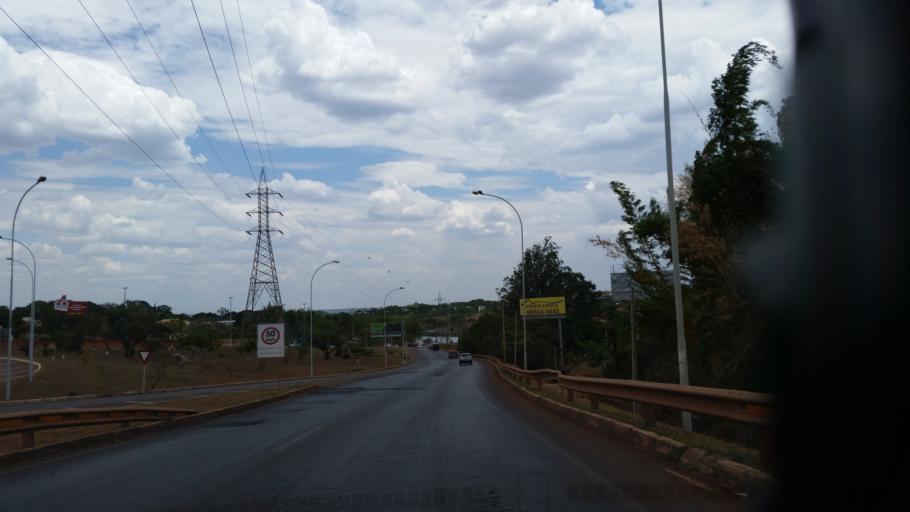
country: BR
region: Federal District
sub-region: Brasilia
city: Brasilia
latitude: -15.7258
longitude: -47.8971
